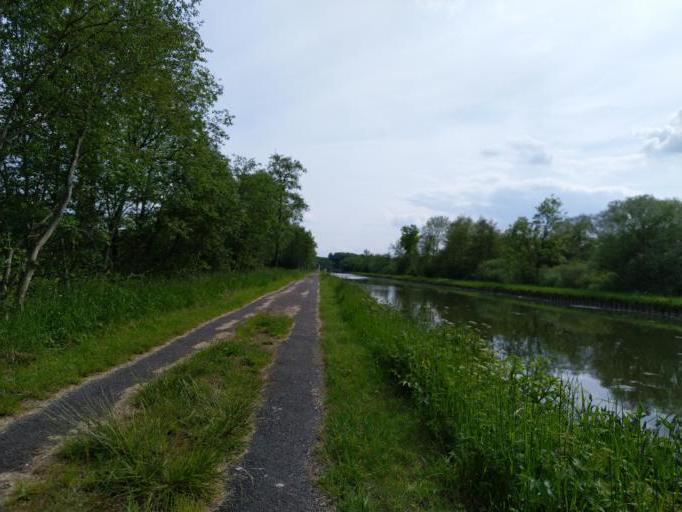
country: FR
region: Picardie
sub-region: Departement de l'Aisne
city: Etreux
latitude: 49.9649
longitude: 3.6187
